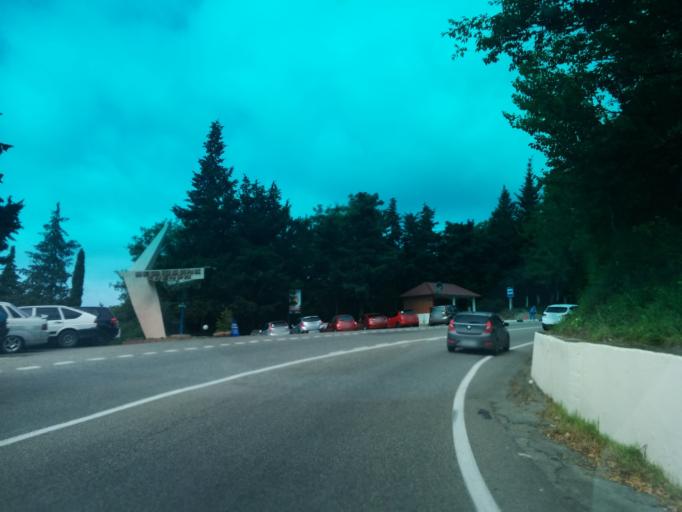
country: RU
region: Krasnodarskiy
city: Nebug
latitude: 44.1735
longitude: 38.9707
